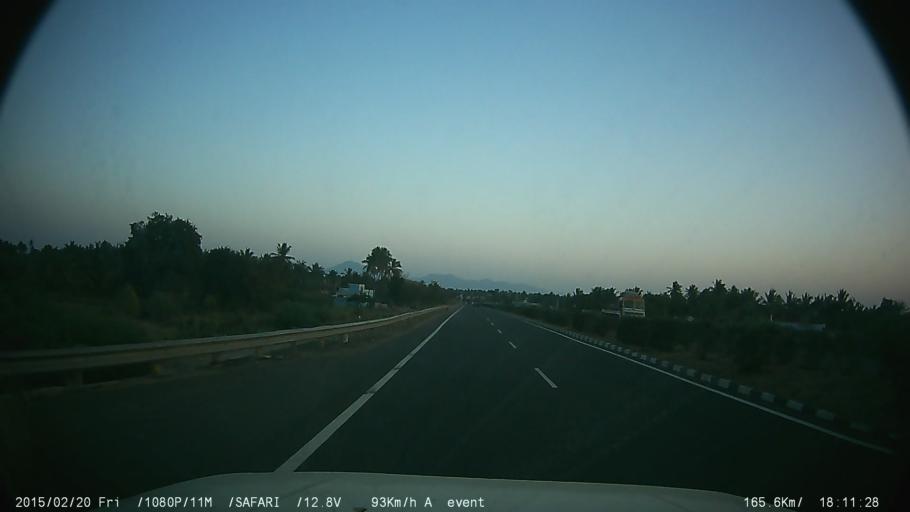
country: IN
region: Tamil Nadu
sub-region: Dharmapuri
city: Palakkodu
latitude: 12.2636
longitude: 78.1972
